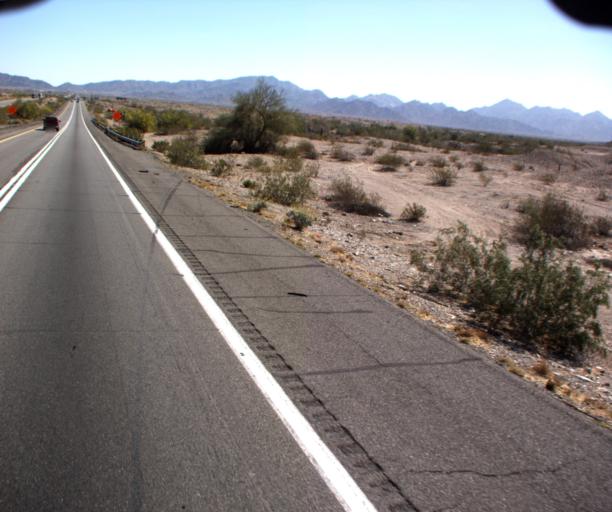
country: US
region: Arizona
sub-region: La Paz County
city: Ehrenberg
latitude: 33.6094
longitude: -114.4851
